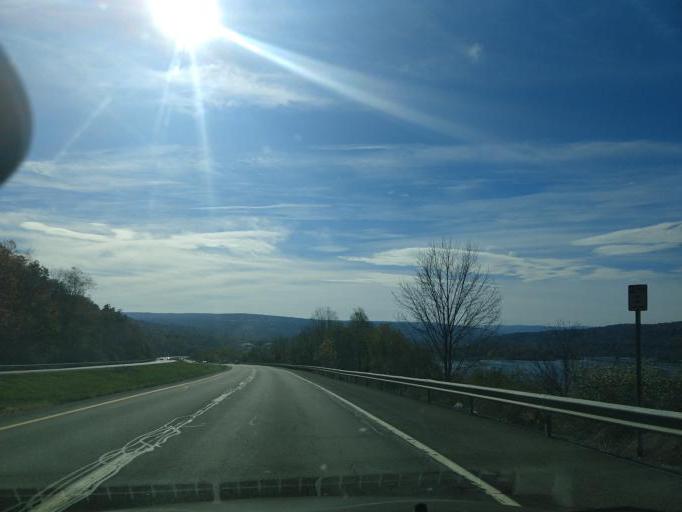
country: US
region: New York
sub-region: Tompkins County
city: Cayuga Heights
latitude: 42.4735
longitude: -76.5012
